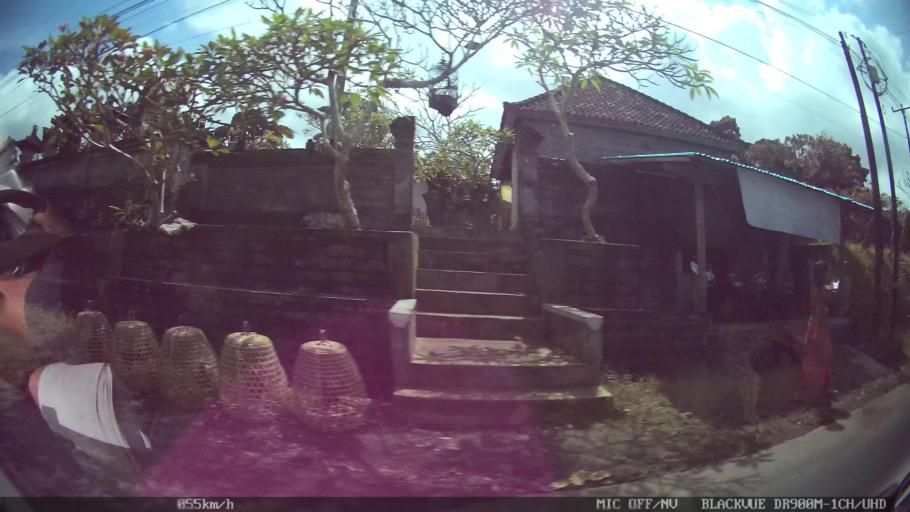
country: ID
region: Bali
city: Banjar Mulung
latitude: -8.4960
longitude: 115.3204
